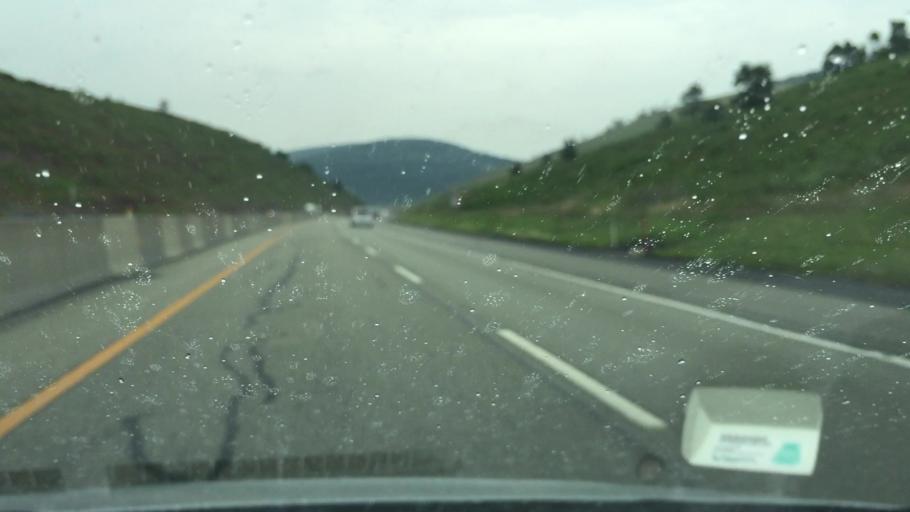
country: US
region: Pennsylvania
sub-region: Somerset County
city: Central City
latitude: 39.9765
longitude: -78.7988
